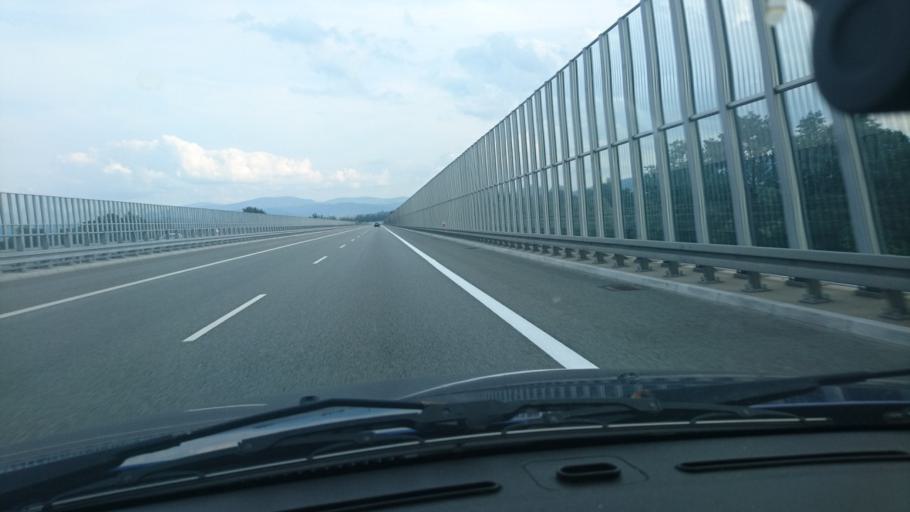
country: PL
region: Silesian Voivodeship
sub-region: Powiat bielski
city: Rybarzowice
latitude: 49.7302
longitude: 19.1166
